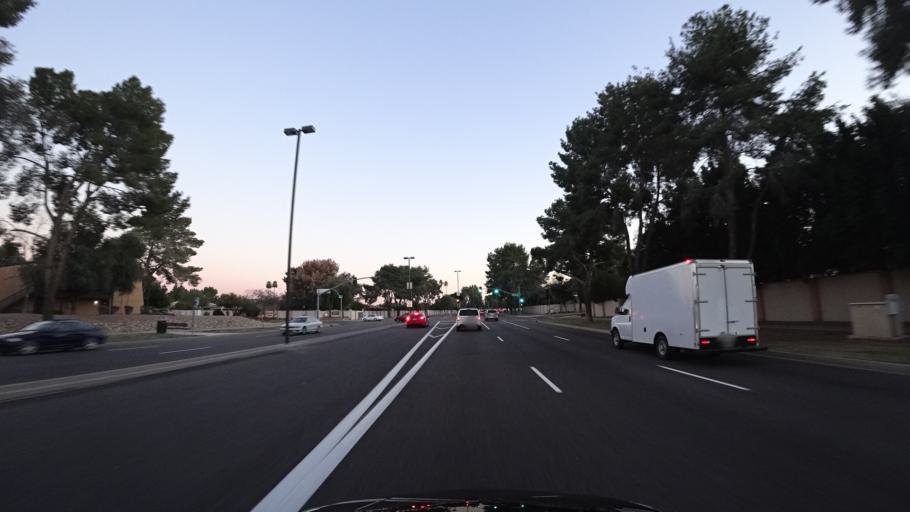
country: US
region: Arizona
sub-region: Maricopa County
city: San Carlos
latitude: 33.3679
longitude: -111.8780
